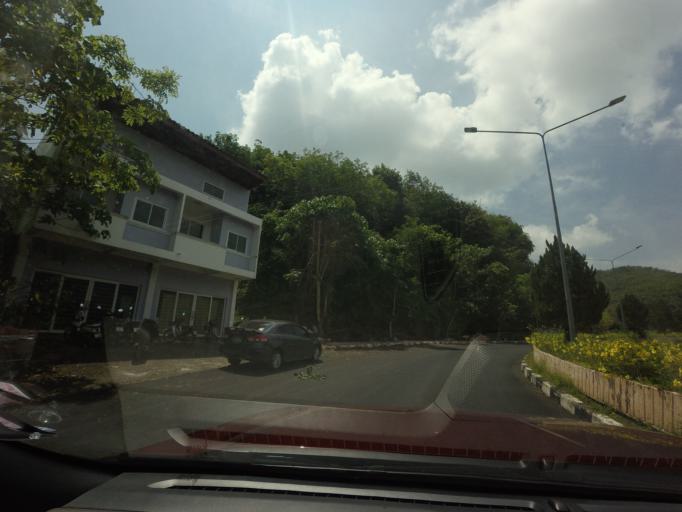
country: TH
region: Yala
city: Betong
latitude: 5.7643
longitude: 101.0482
